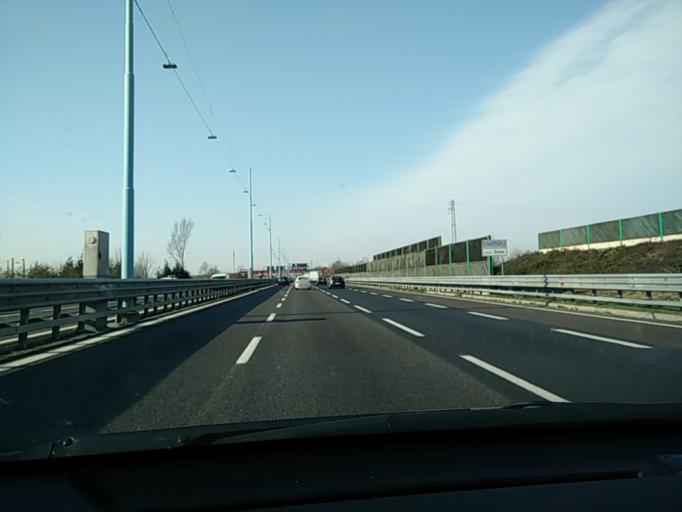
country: IT
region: Veneto
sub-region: Provincia di Venezia
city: Dese
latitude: 45.5310
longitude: 12.2707
